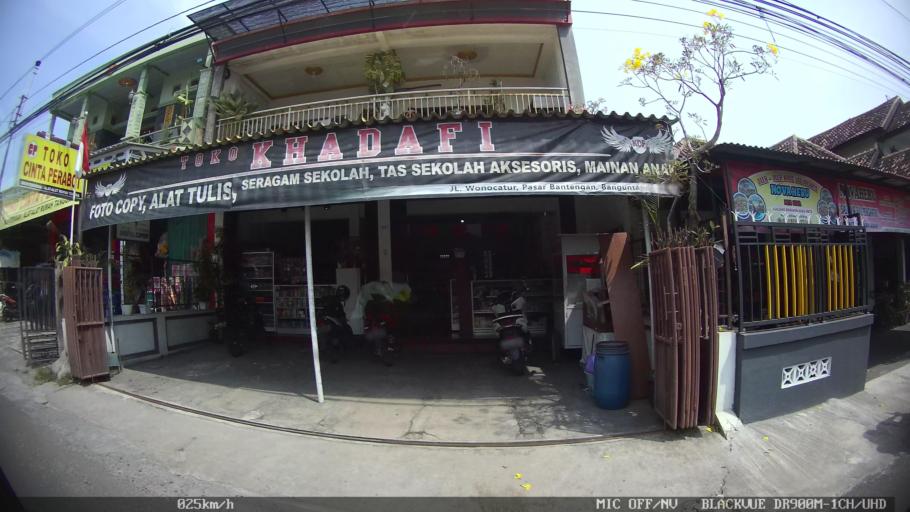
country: ID
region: Daerah Istimewa Yogyakarta
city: Depok
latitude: -7.8028
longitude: 110.4141
